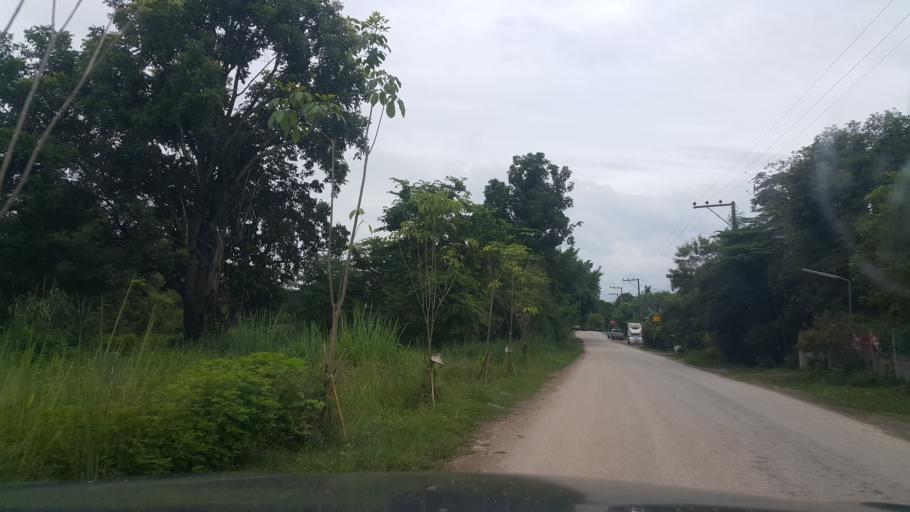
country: TH
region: Chiang Mai
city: San Sai
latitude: 18.9259
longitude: 99.0343
